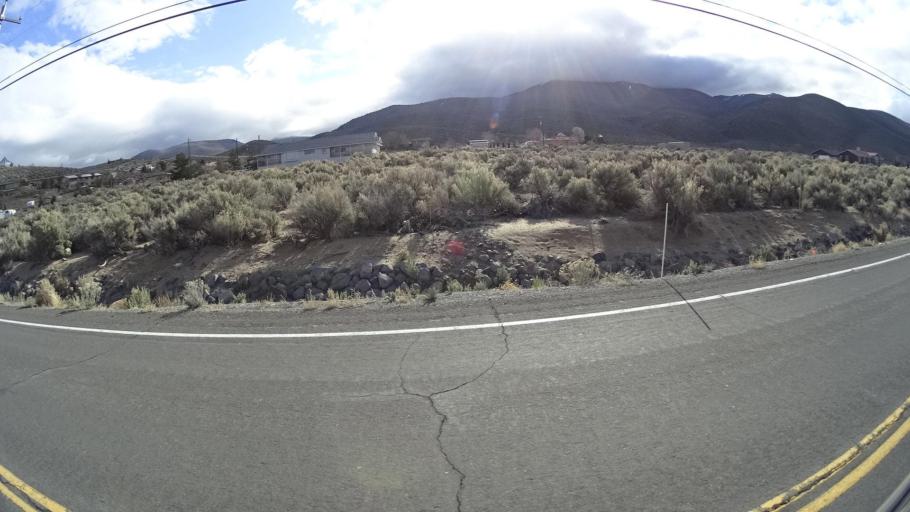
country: US
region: Nevada
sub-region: Storey County
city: Virginia City
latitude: 39.2767
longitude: -119.7567
